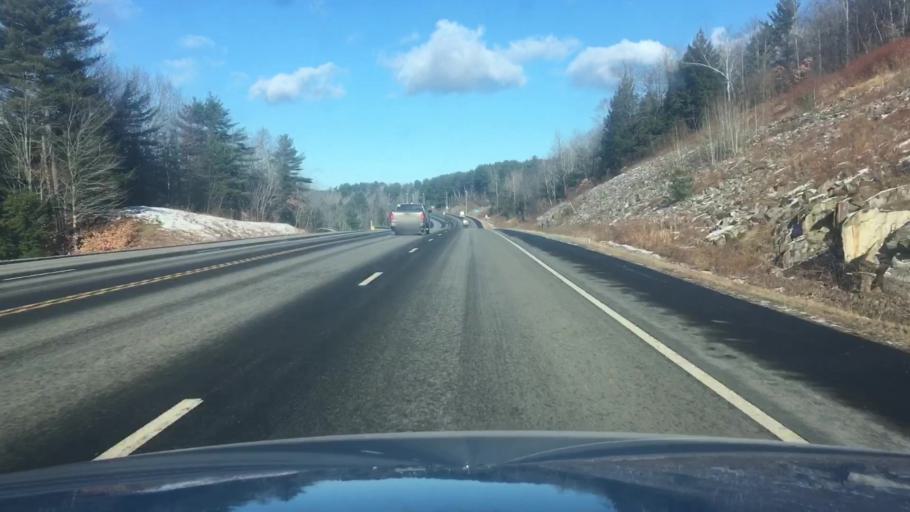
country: US
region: Maine
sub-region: Kennebec County
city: Augusta
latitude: 44.3403
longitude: -69.7677
